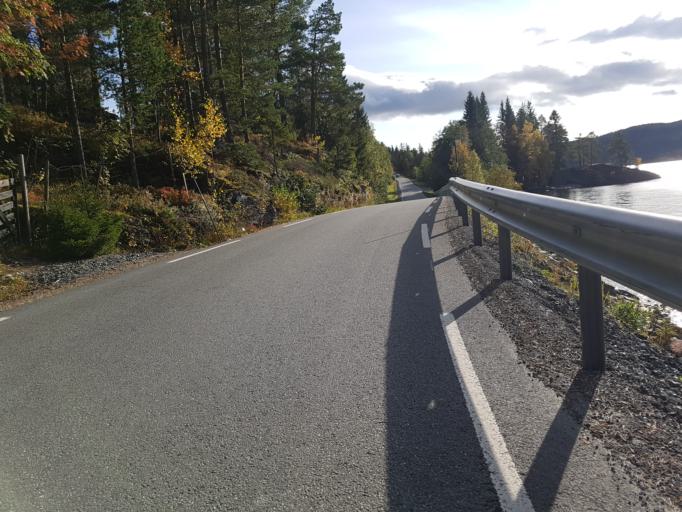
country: NO
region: Sor-Trondelag
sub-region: Malvik
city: Malvik
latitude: 63.3566
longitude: 10.6394
